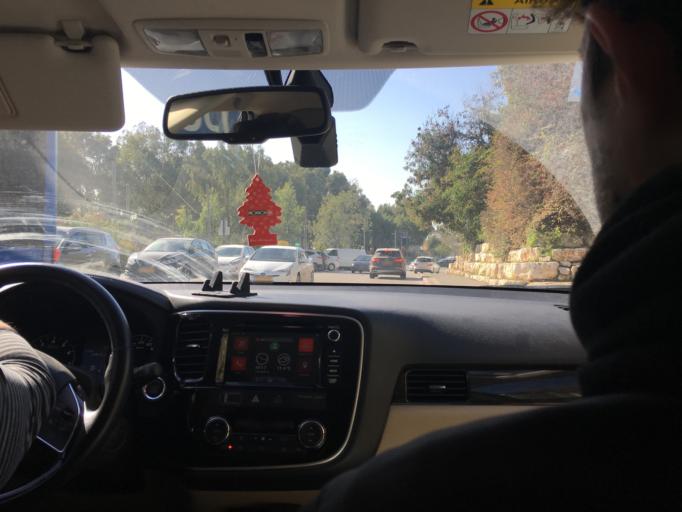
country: IL
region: Tel Aviv
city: Ramat HaSharon
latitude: 32.1405
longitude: 34.8461
